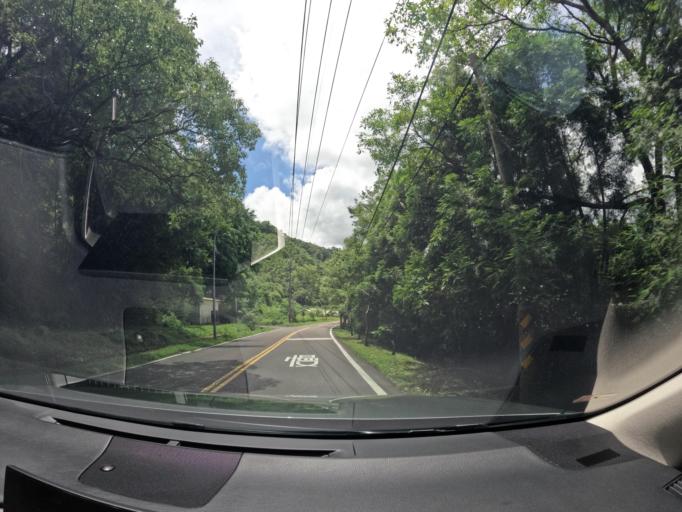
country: TW
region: Taiwan
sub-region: Miaoli
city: Miaoli
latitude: 24.6125
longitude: 121.0045
